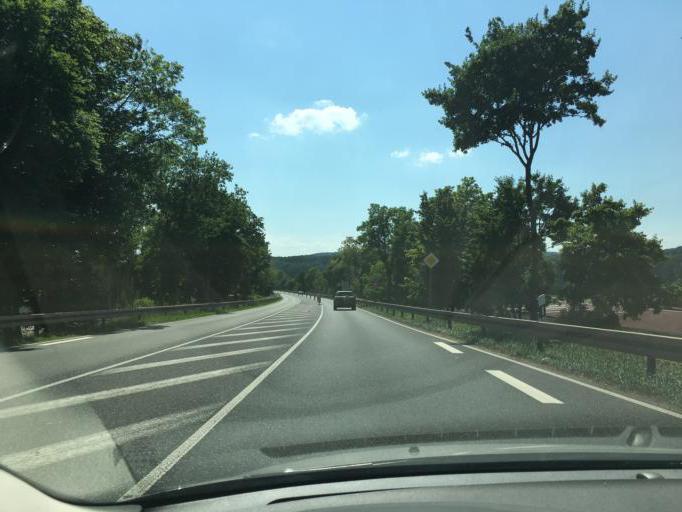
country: DE
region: Hesse
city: Bebra
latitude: 50.9777
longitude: 9.7833
